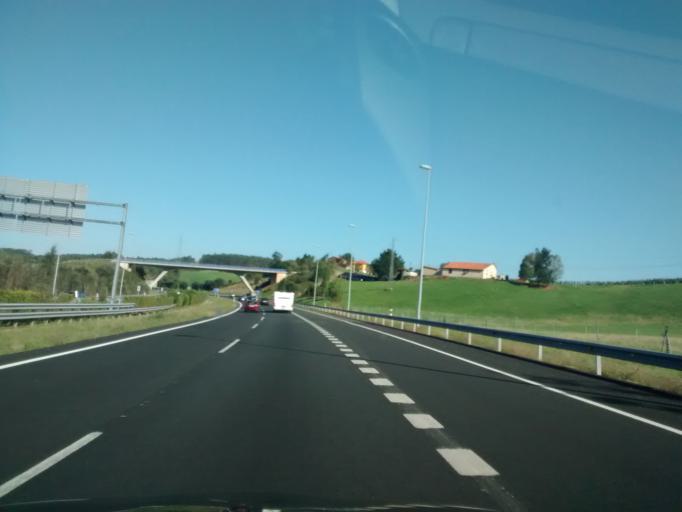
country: ES
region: Cantabria
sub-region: Provincia de Cantabria
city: Cabezon de la Sal
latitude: 43.3163
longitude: -4.2456
